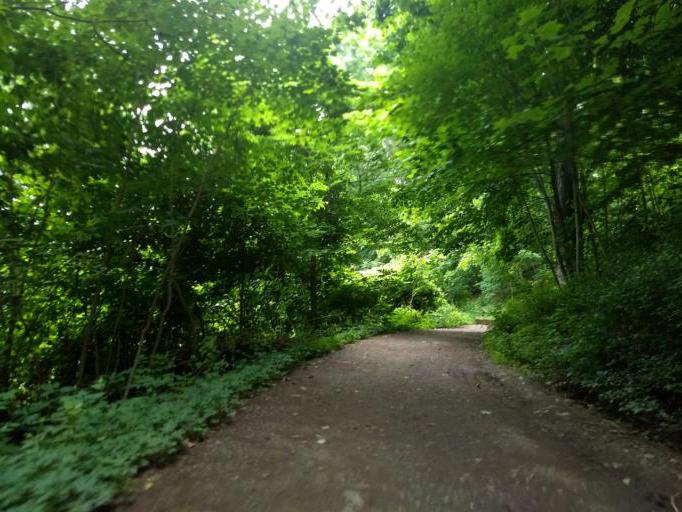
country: US
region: Pennsylvania
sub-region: Allegheny County
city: Wilkinsburg
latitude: 40.4382
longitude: -79.9009
